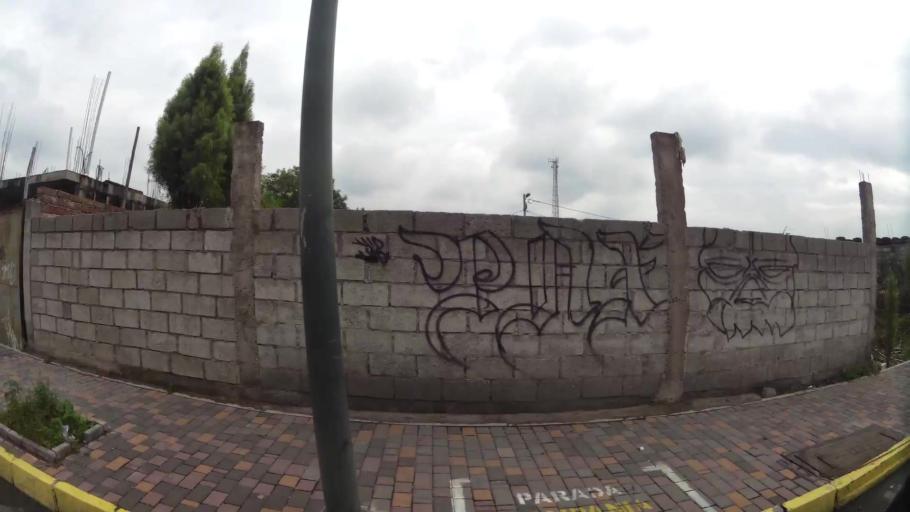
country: EC
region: Pichincha
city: Sangolqui
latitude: -0.3137
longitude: -78.4734
